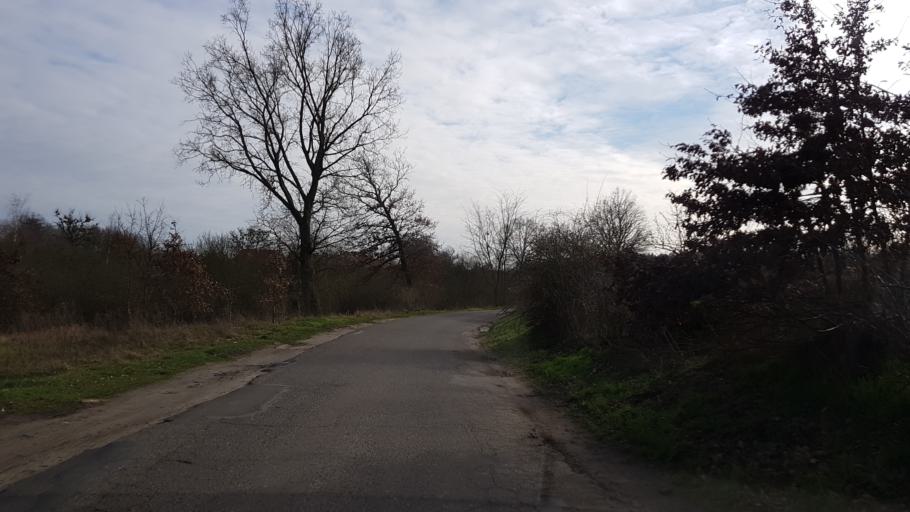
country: PL
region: West Pomeranian Voivodeship
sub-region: Powiat policki
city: Dobra
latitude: 53.5087
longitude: 14.3511
